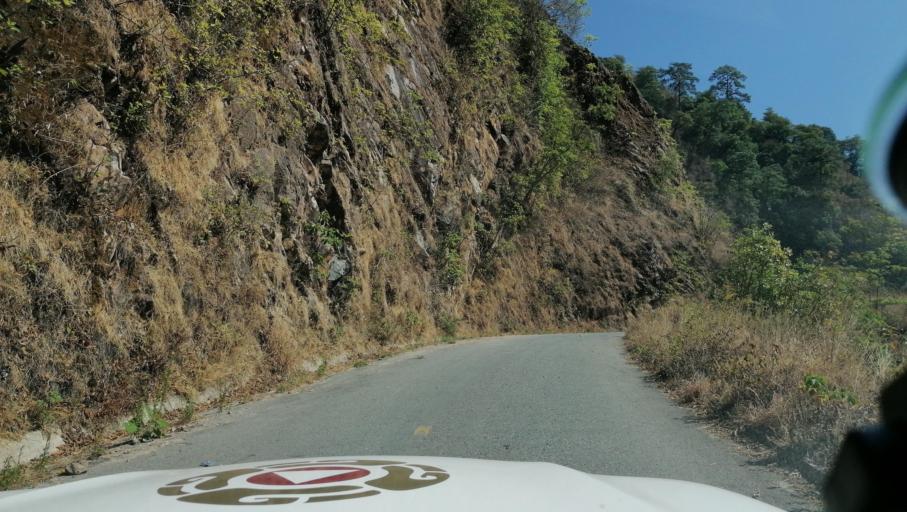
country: MX
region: Chiapas
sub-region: Cacahoatan
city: Benito Juarez
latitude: 15.1838
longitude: -92.1903
